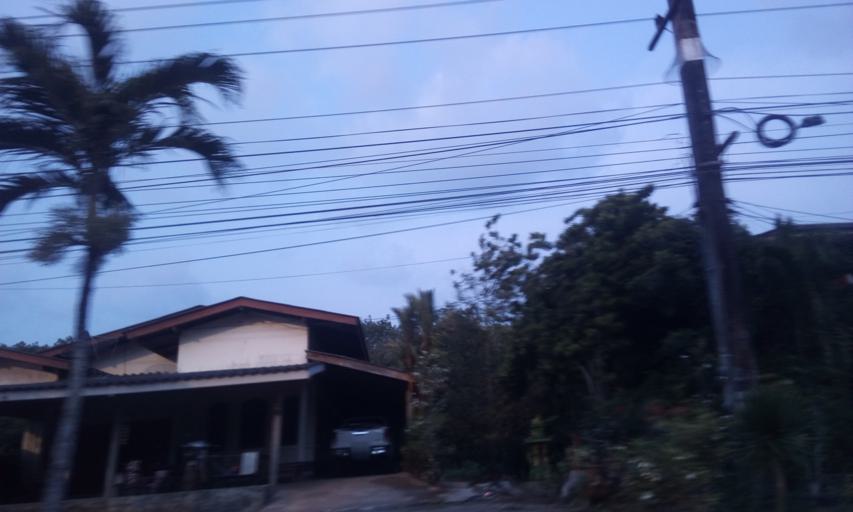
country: TH
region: Trat
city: Laem Ngop
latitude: 12.2506
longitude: 102.2924
